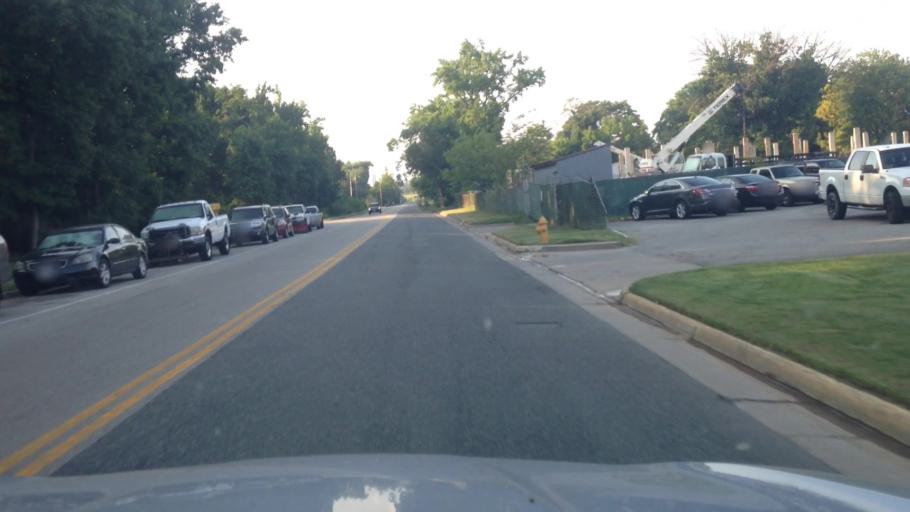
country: US
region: Virginia
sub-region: Prince William County
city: Woodbridge
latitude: 38.6535
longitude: -77.2462
